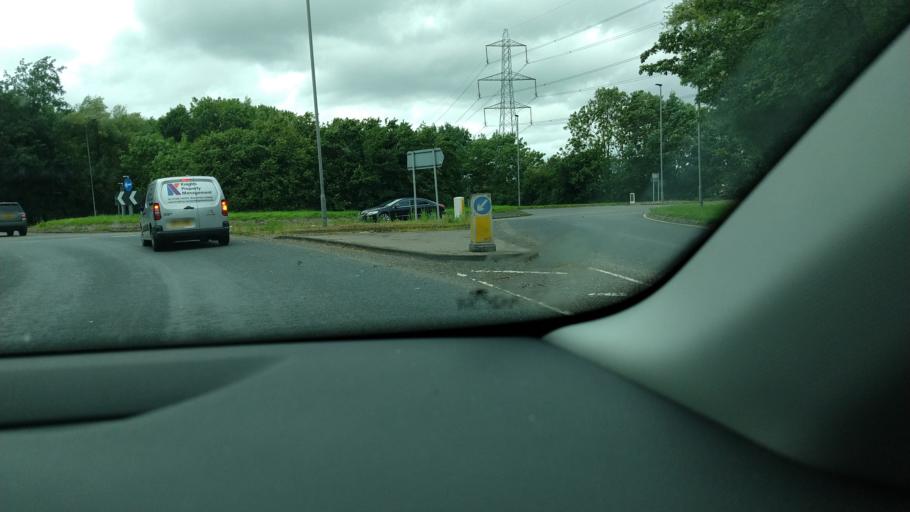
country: GB
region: England
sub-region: North Yorkshire
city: Camblesforth
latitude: 53.7292
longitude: -0.9924
